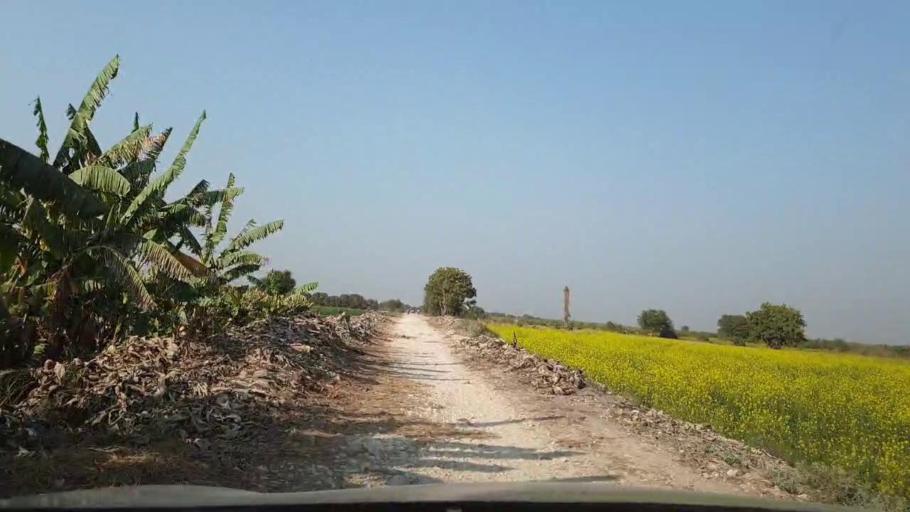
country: PK
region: Sindh
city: Tando Allahyar
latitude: 25.5721
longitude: 68.7951
